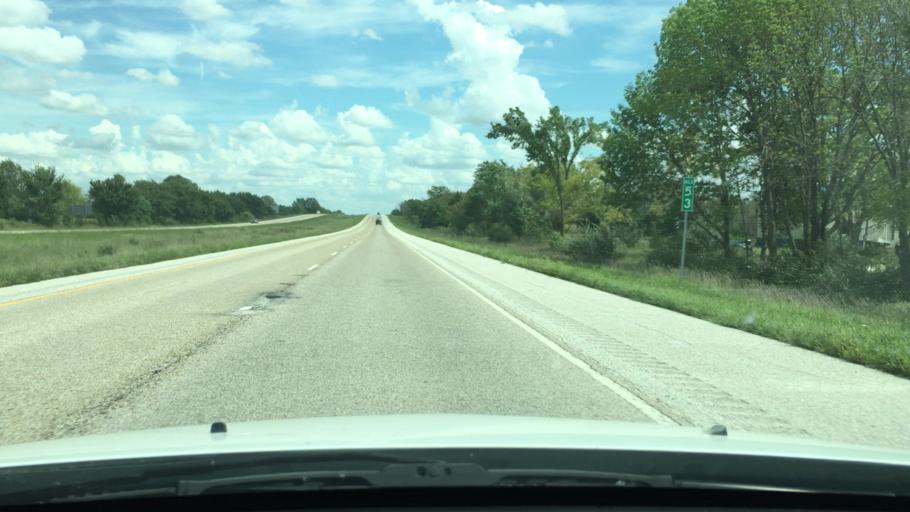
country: US
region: Illinois
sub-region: Scott County
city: Winchester
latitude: 39.6810
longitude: -90.4373
